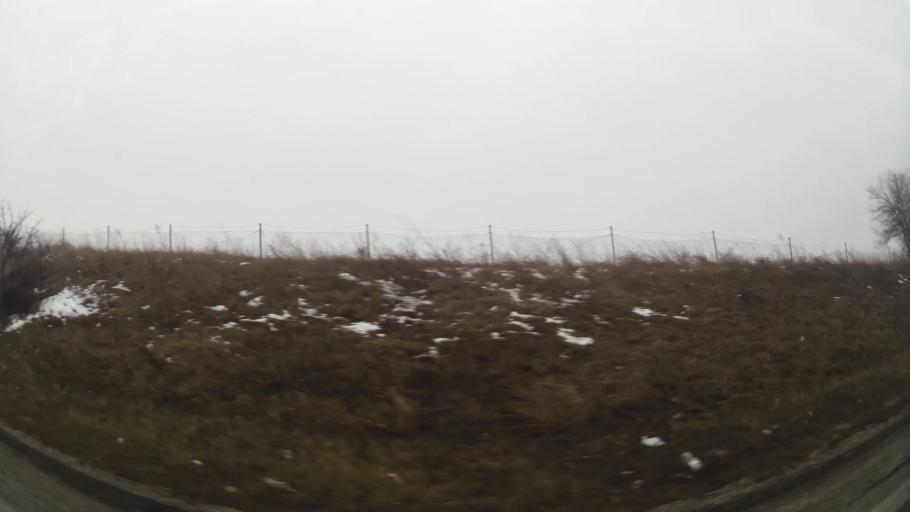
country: MK
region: Petrovec
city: Petrovec
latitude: 41.9483
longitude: 21.6307
